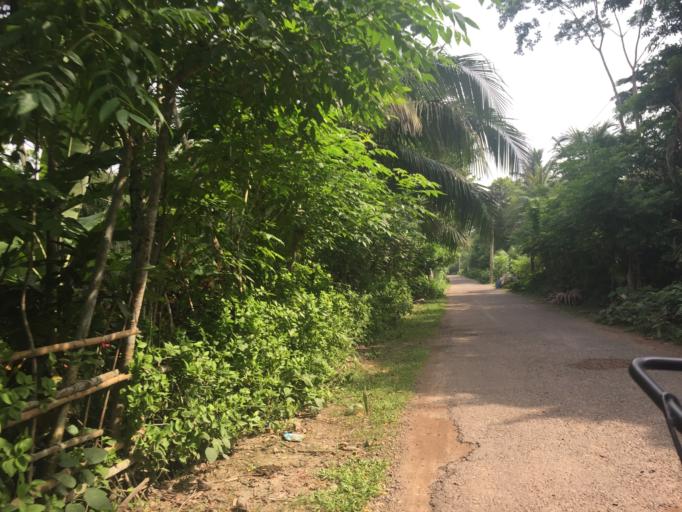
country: BD
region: Barisal
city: Mathba
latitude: 22.2215
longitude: 89.9161
